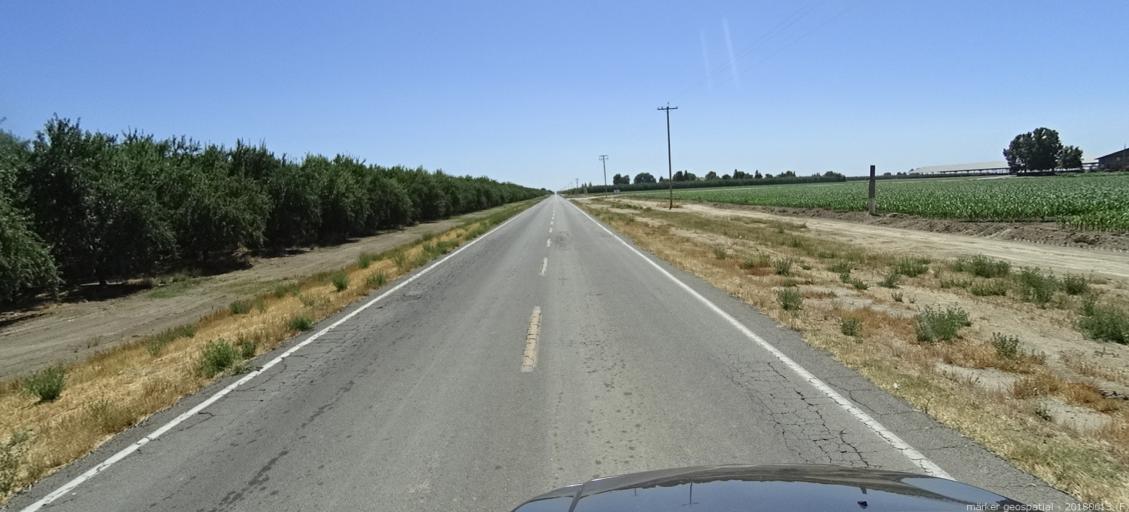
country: US
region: California
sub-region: Madera County
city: Chowchilla
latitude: 37.0181
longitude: -120.3749
